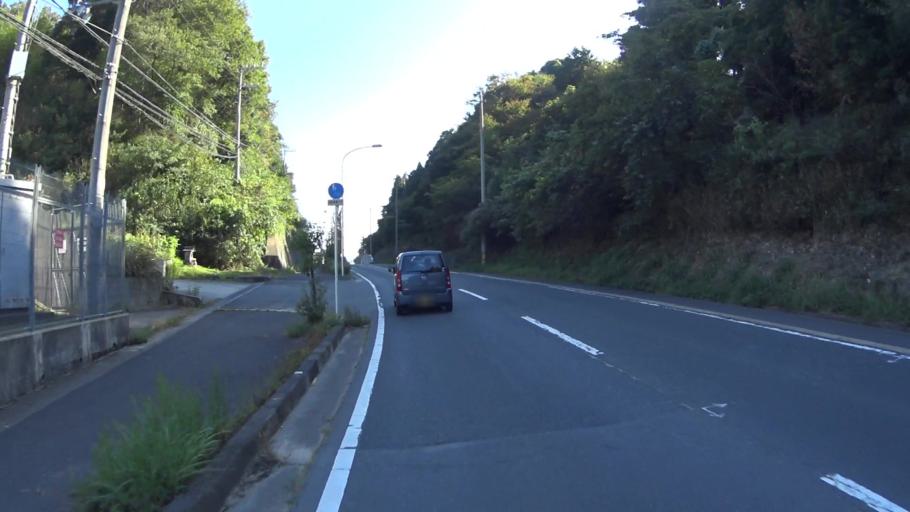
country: JP
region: Kyoto
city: Miyazu
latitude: 35.6345
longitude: 135.0538
